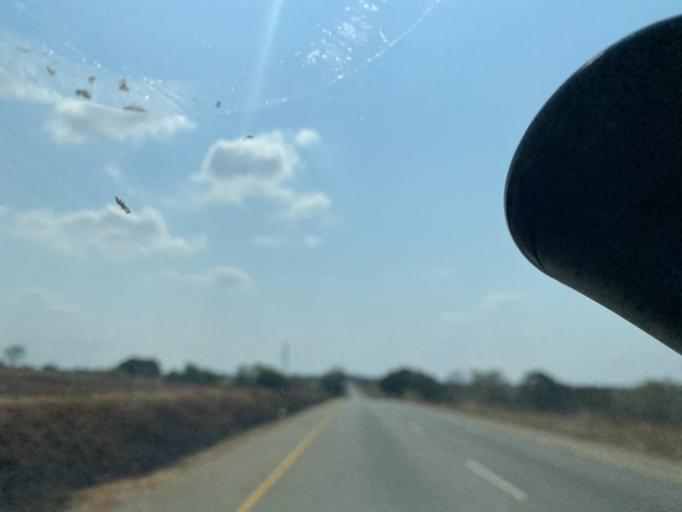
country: ZM
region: Lusaka
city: Chongwe
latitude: -15.5288
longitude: 28.6134
